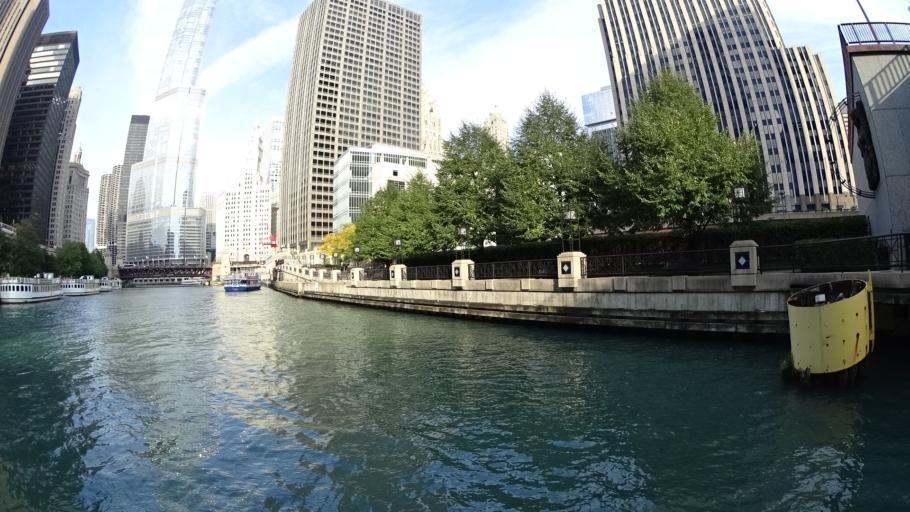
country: US
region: Illinois
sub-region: Cook County
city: Chicago
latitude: 41.8888
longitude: -87.6208
